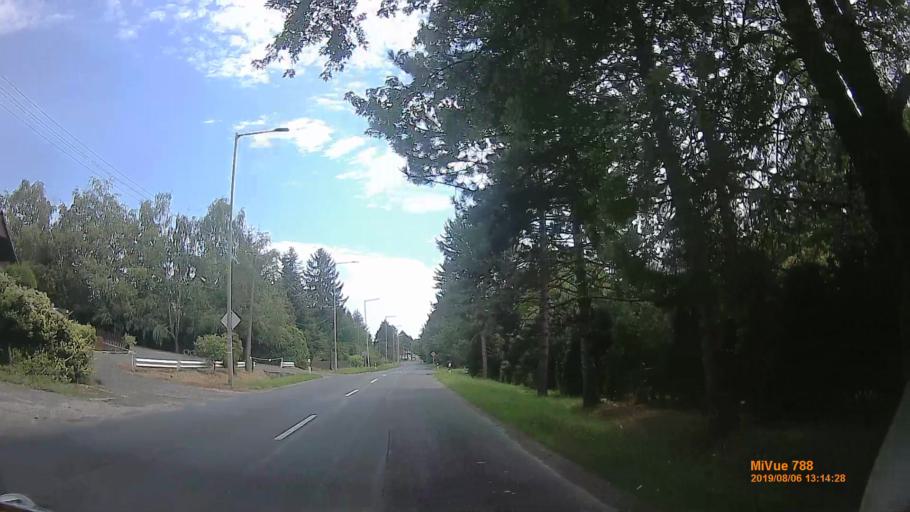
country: HU
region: Vas
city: Koszeg
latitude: 47.4045
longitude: 16.5336
